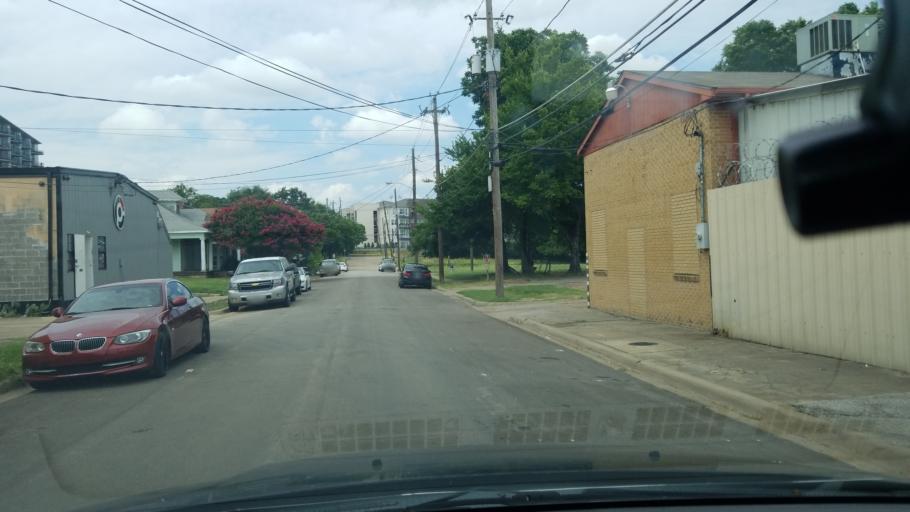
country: US
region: Texas
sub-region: Dallas County
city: Dallas
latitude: 32.7711
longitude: -96.7937
